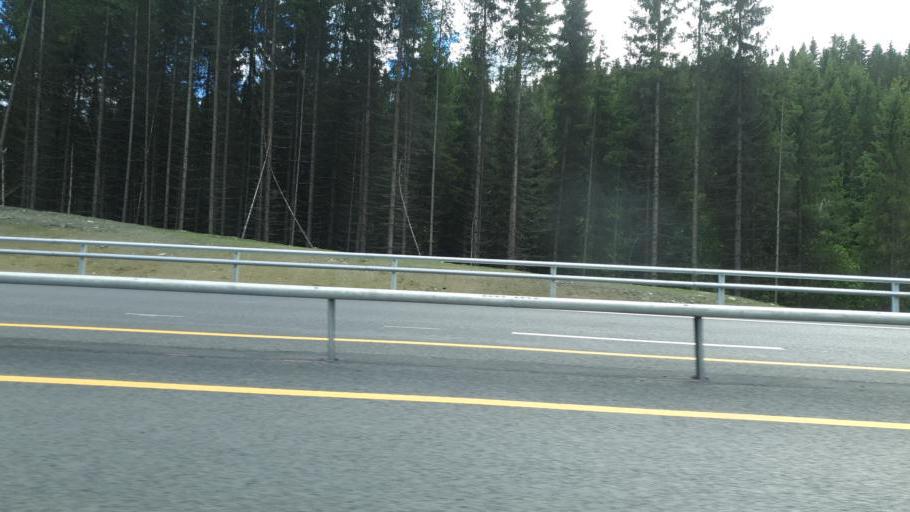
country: NO
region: Sor-Trondelag
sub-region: Midtre Gauldal
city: Storen
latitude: 62.9329
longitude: 10.1856
